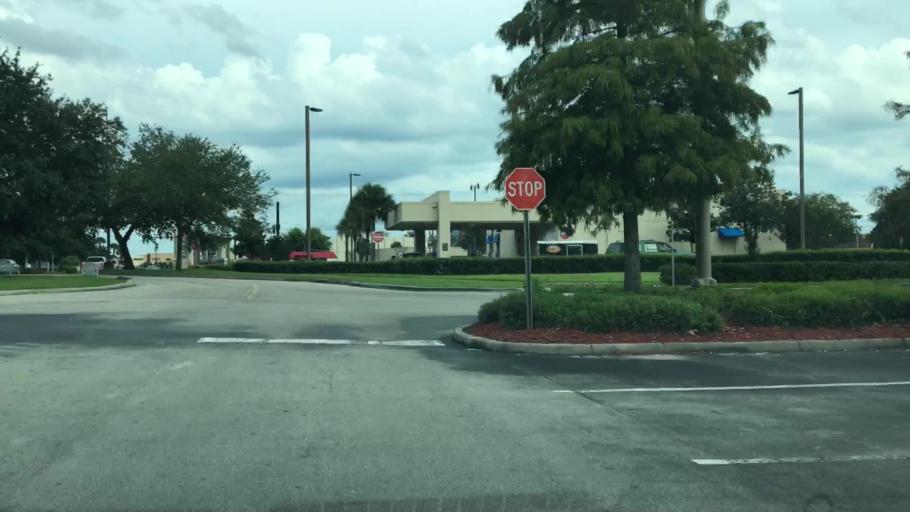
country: US
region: Florida
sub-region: Seminole County
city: Lake Mary
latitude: 28.7602
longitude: -81.2872
